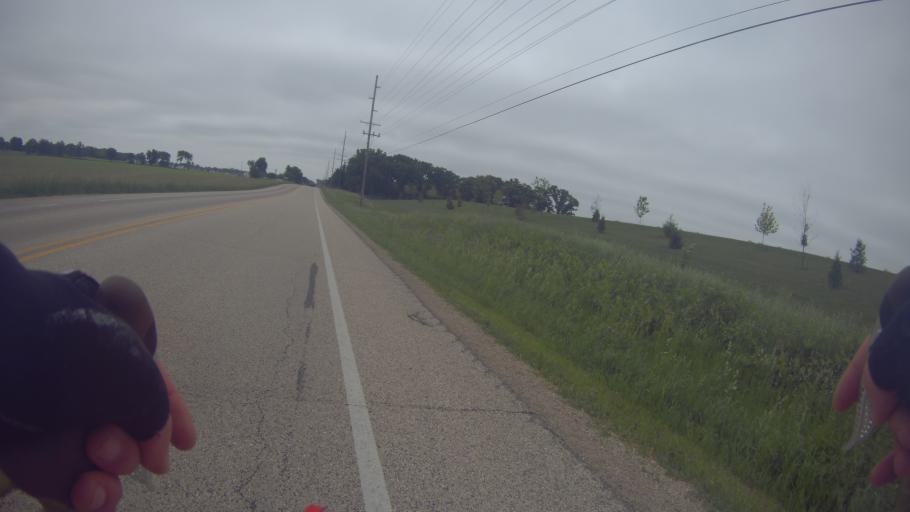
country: US
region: Wisconsin
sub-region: Green County
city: Brooklyn
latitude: 42.8666
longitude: -89.3689
